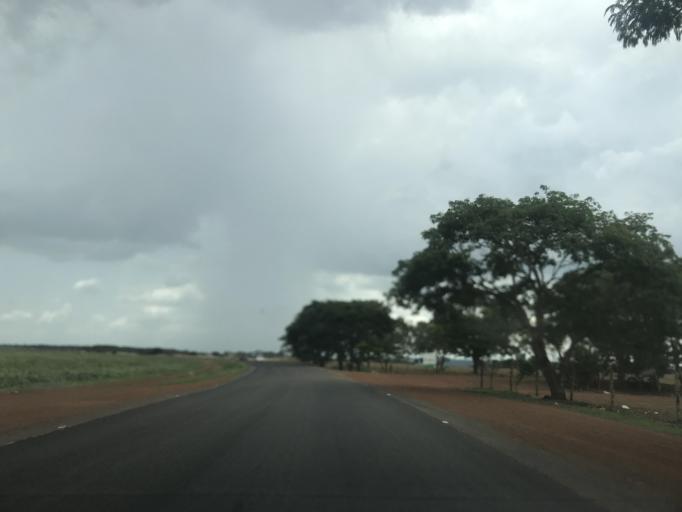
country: BR
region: Goias
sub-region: Vianopolis
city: Vianopolis
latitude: -16.8643
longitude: -48.5489
